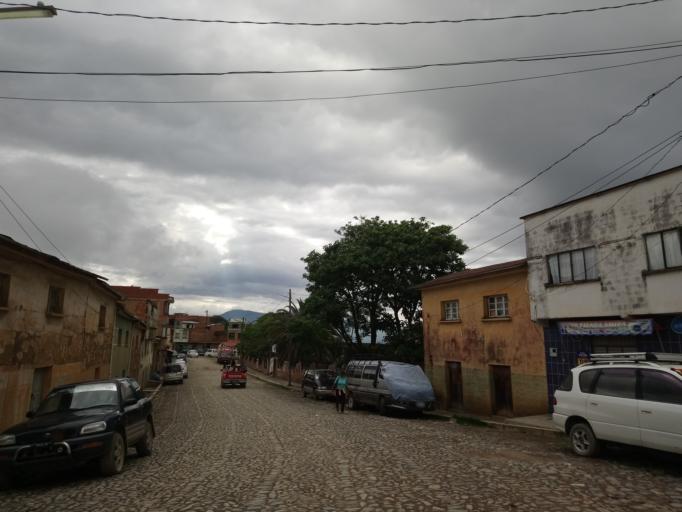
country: BO
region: La Paz
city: Coripata
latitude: -16.2699
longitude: -67.6417
